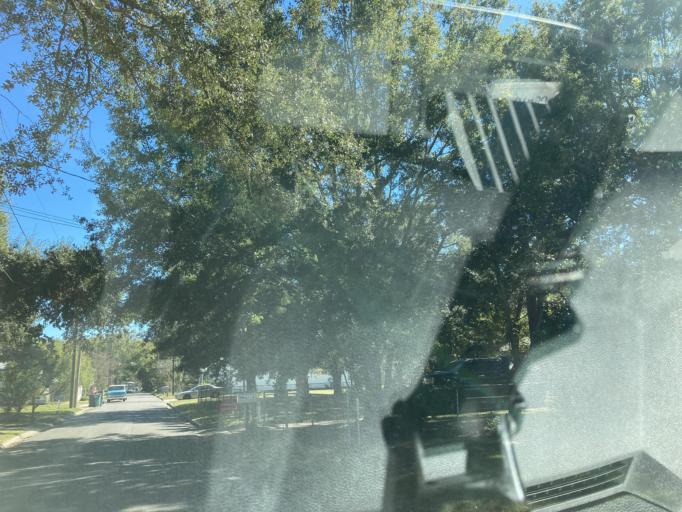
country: US
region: Mississippi
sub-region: Jackson County
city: Ocean Springs
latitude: 30.4126
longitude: -88.8241
